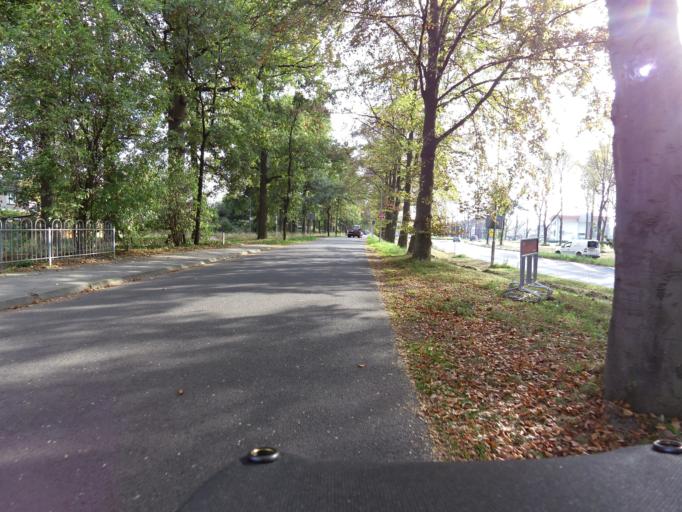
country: NL
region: Gelderland
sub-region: Gemeente Wageningen
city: Wageningen
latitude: 51.9748
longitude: 5.6513
